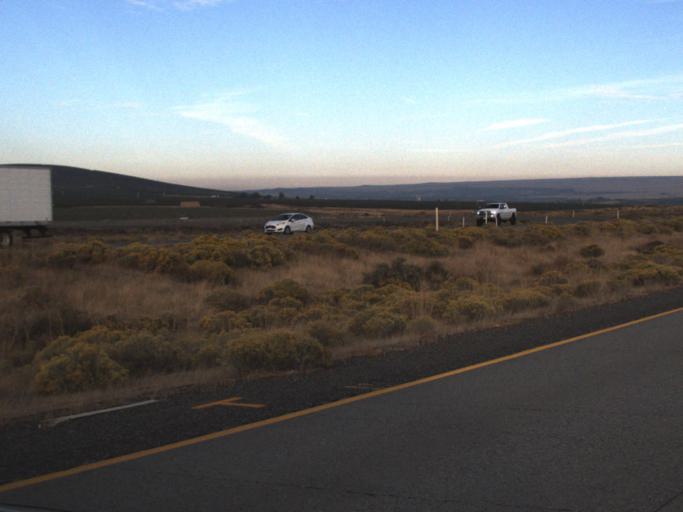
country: US
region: Washington
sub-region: Benton County
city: West Richland
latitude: 46.2466
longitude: -119.3642
